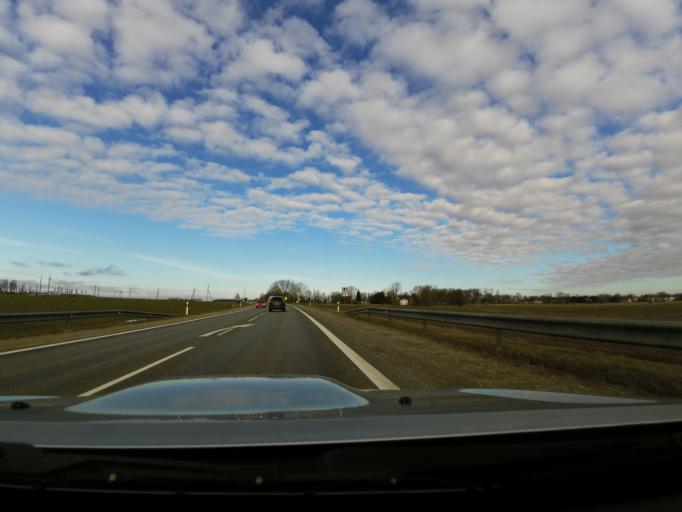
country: LT
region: Siauliu apskritis
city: Pakruojis
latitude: 55.7962
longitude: 24.0216
